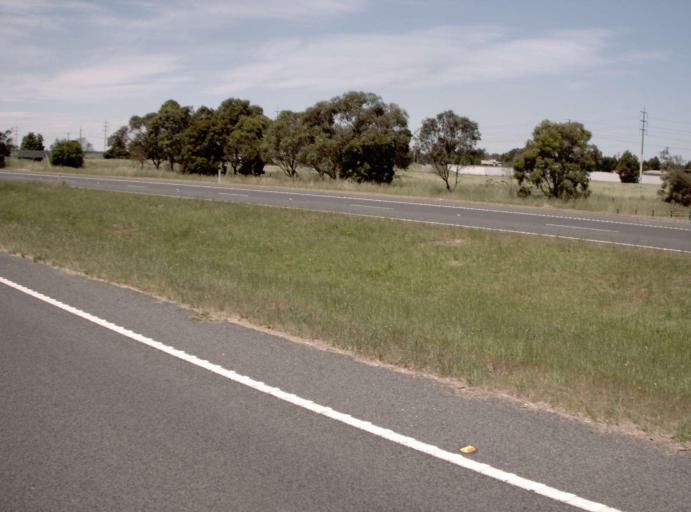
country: AU
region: Victoria
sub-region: Latrobe
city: Morwell
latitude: -38.2417
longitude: 146.4453
